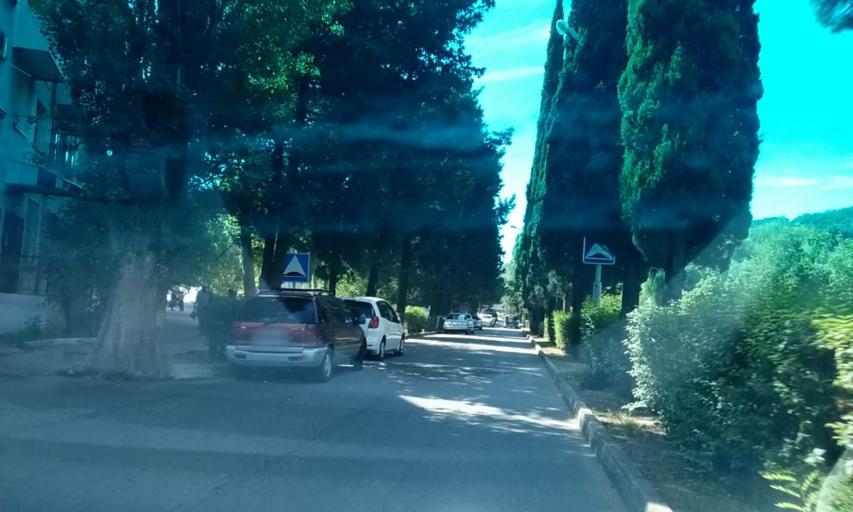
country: RU
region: Krasnodarskiy
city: Tuapse
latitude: 44.1080
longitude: 39.0606
